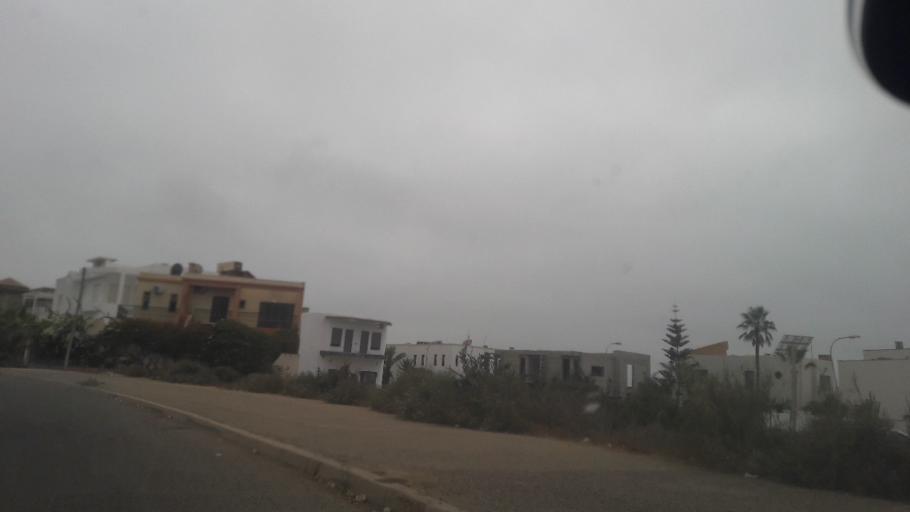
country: MA
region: Souss-Massa-Draa
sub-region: Agadir-Ida-ou-Tnan
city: Agadir
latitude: 30.3928
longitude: -9.5955
